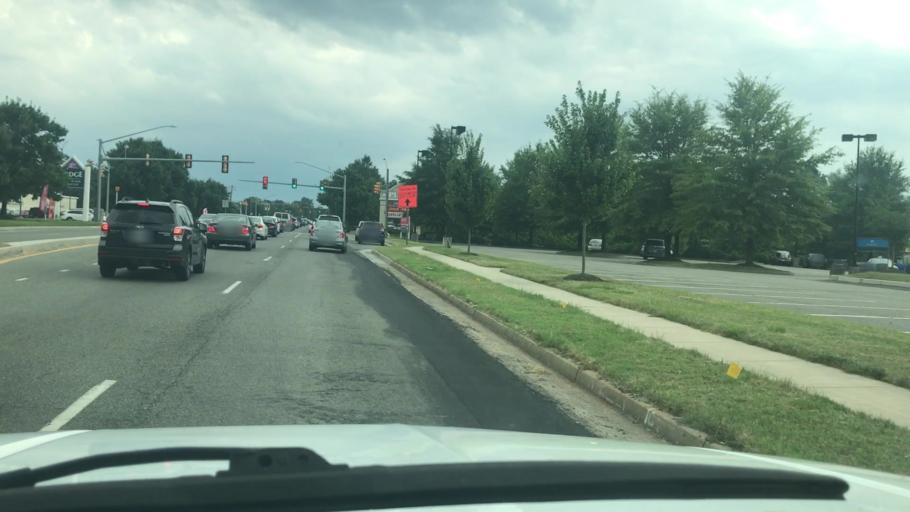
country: US
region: Virginia
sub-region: Henrico County
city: Tuckahoe
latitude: 37.6048
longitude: -77.5647
